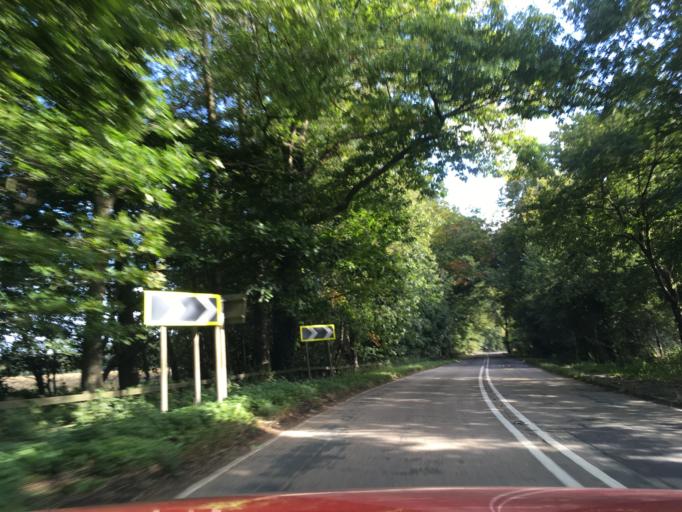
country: GB
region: England
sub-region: Hampshire
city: Old Basing
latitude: 51.2075
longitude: -1.0488
